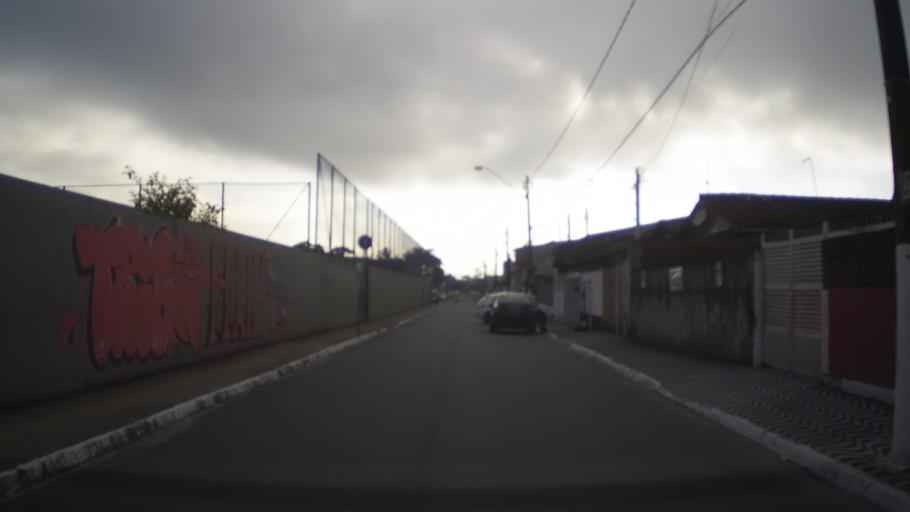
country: BR
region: Sao Paulo
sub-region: Praia Grande
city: Praia Grande
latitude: -24.0145
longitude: -46.4663
